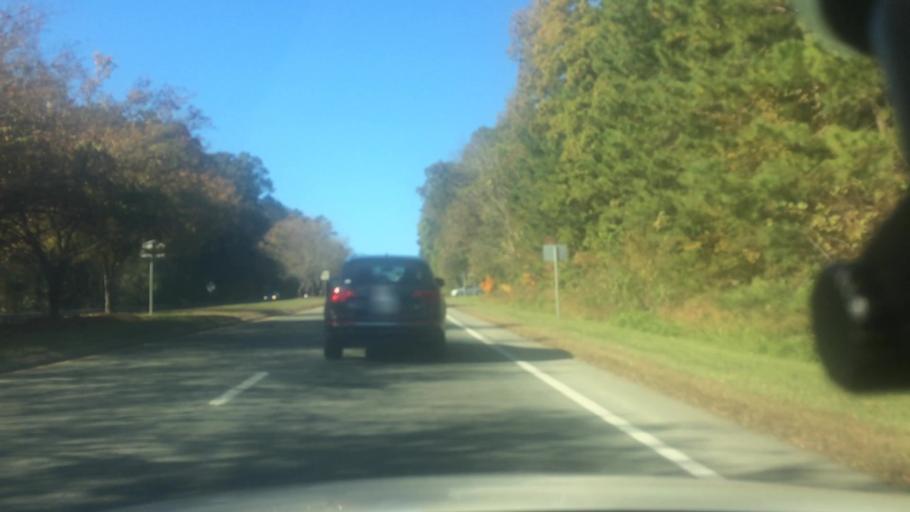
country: US
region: North Carolina
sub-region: Orange County
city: Chapel Hill
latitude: 35.8974
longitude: -79.0393
